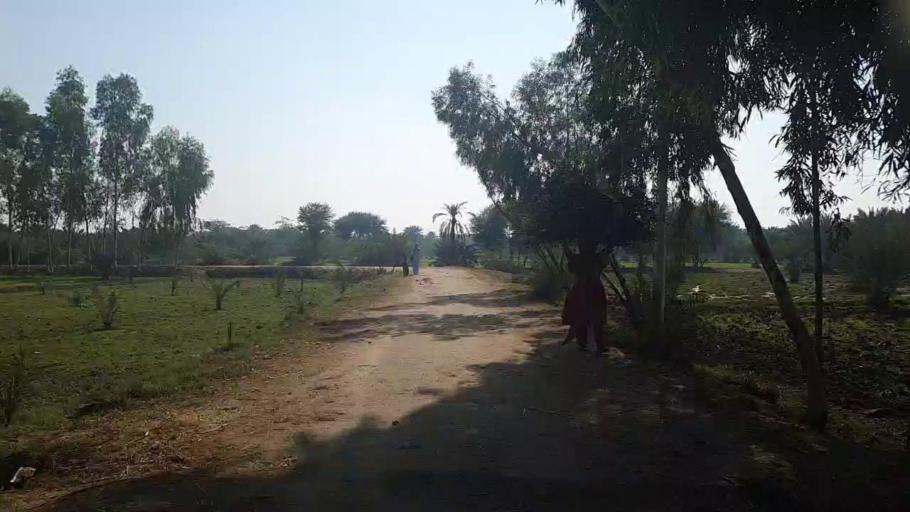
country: PK
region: Sindh
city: Kot Diji
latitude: 27.4318
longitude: 68.7219
